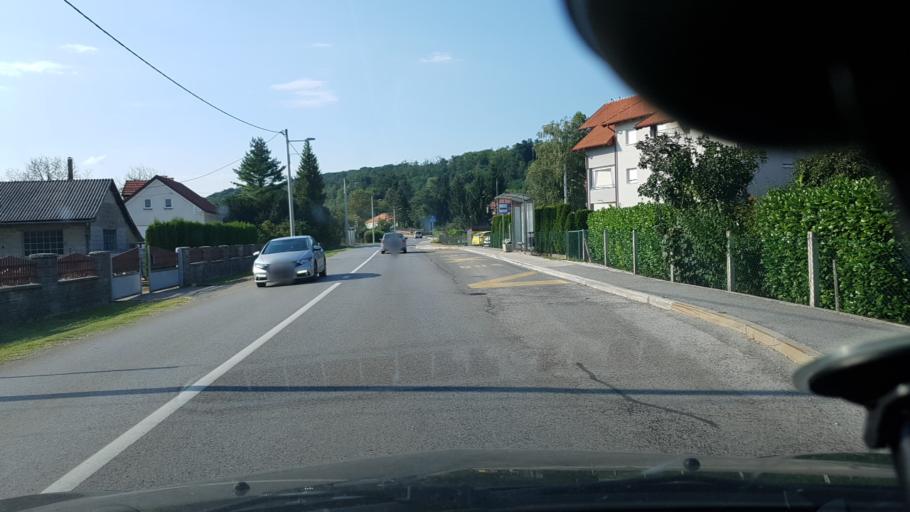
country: HR
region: Zagrebacka
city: Brdovec
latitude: 45.8717
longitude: 15.7524
